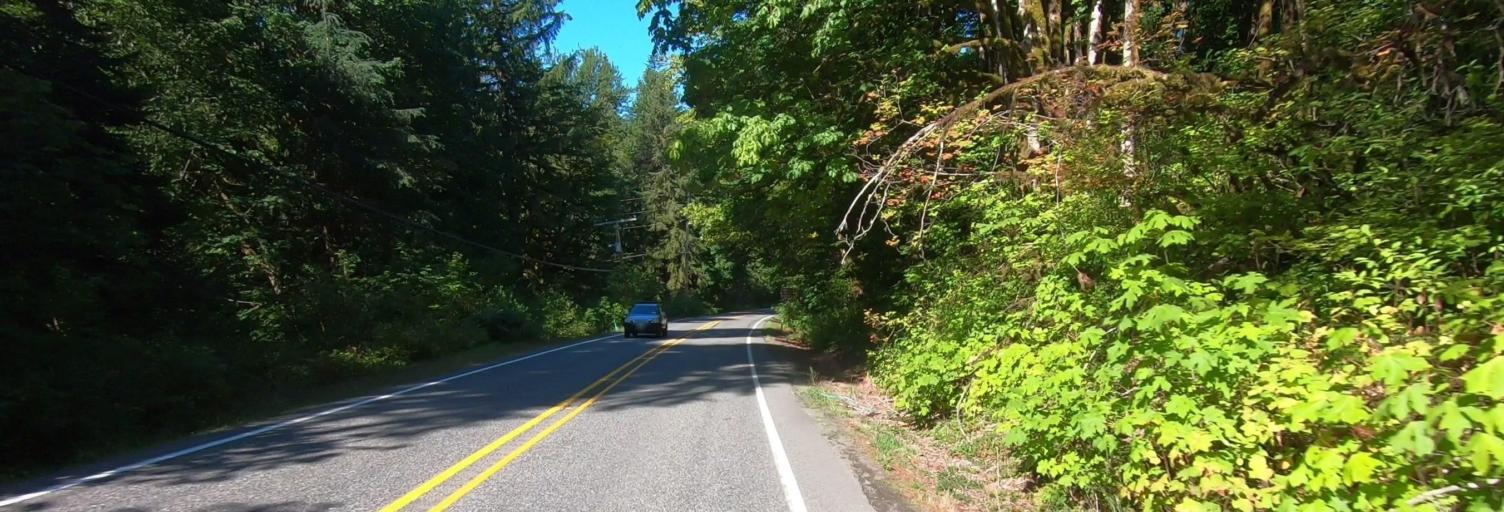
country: US
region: Washington
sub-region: Whatcom County
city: Peaceful Valley
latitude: 48.8904
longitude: -121.9382
